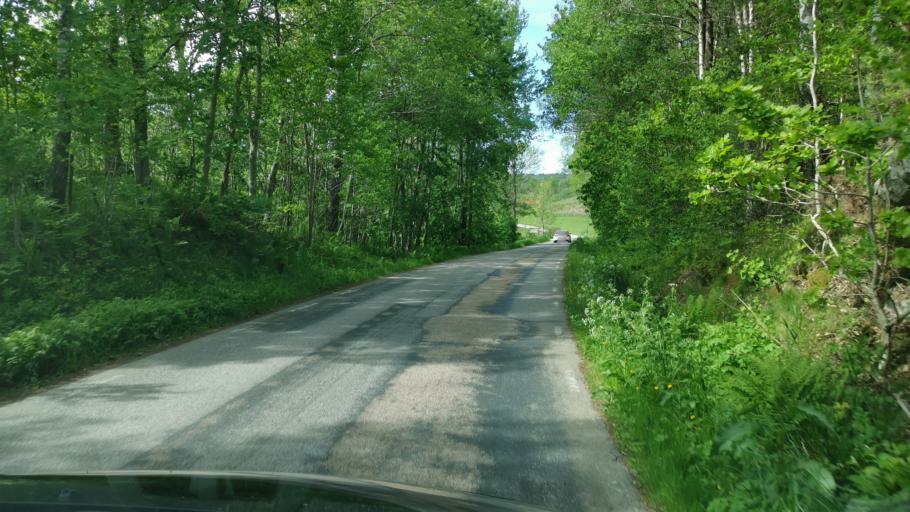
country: SE
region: Vaestra Goetaland
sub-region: Orust
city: Henan
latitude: 58.2679
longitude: 11.6061
